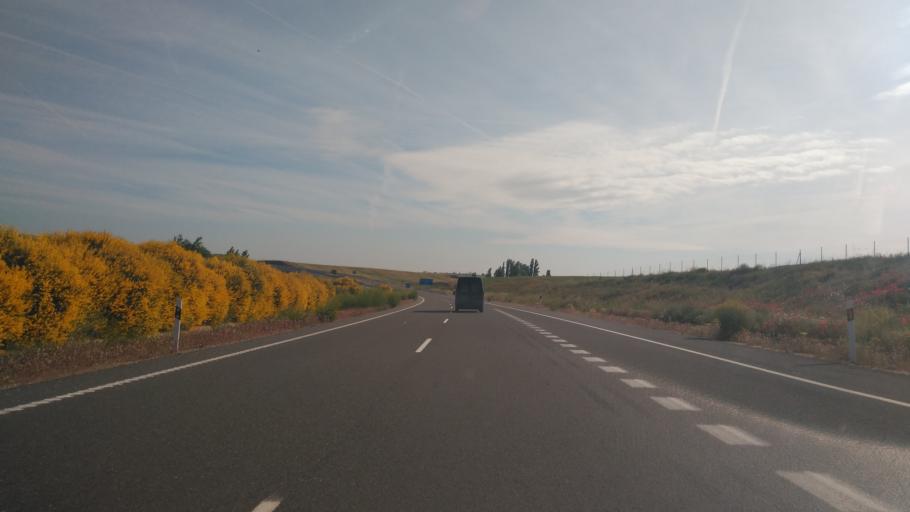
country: ES
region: Castille and Leon
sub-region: Provincia de Salamanca
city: Monterrubio de Armuna
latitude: 41.0339
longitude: -5.6705
